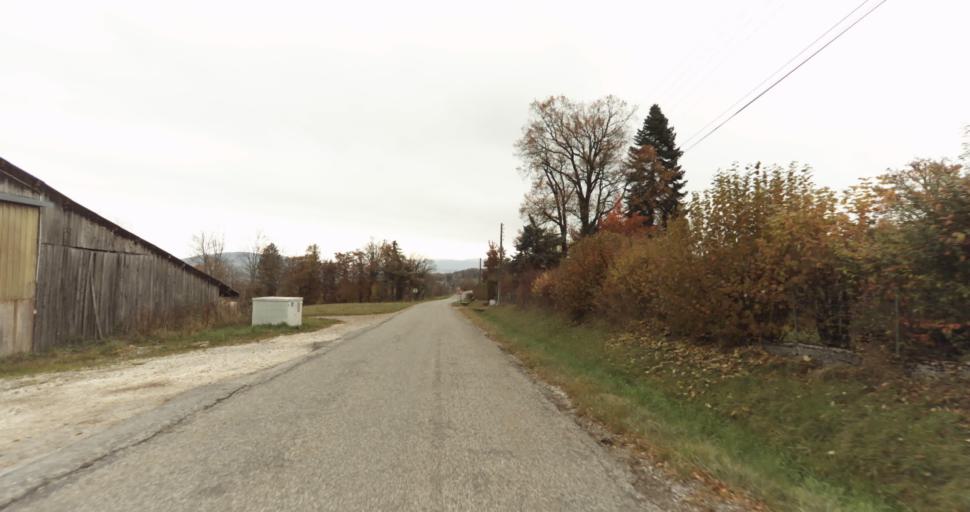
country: FR
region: Rhone-Alpes
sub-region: Departement de la Haute-Savoie
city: Saint-Martin-Bellevue
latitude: 45.9575
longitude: 6.1445
